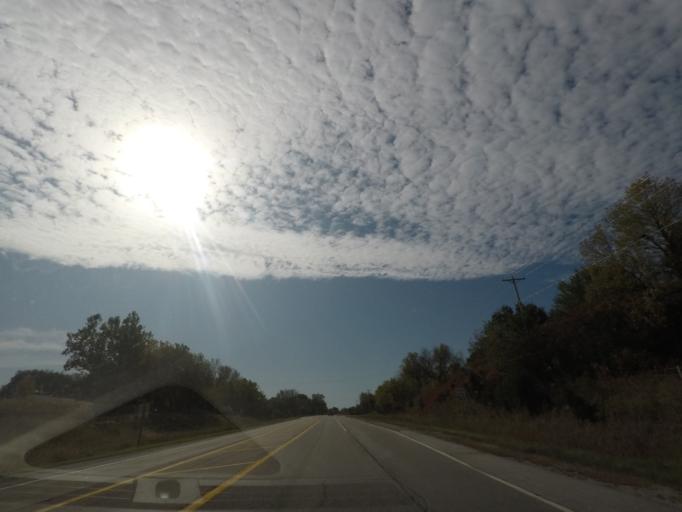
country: US
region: Iowa
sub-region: Story County
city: Gilbert
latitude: 42.0794
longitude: -93.6207
